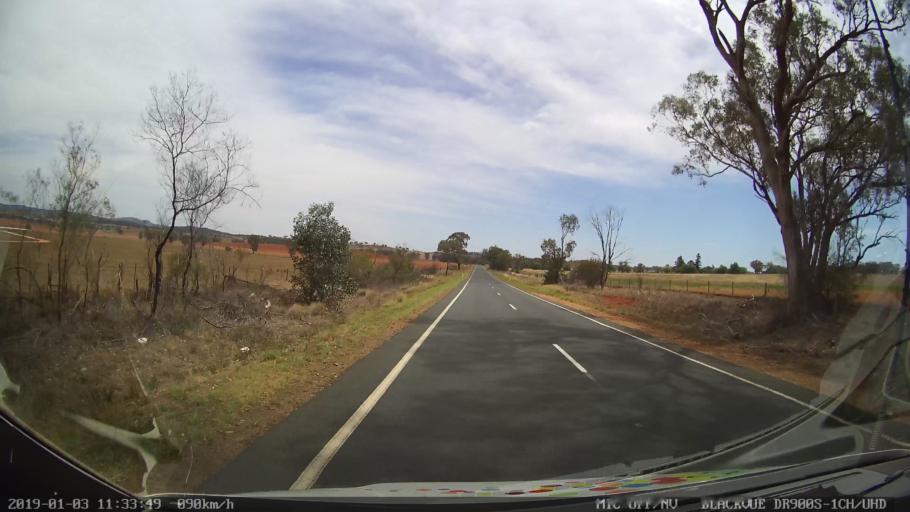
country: AU
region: New South Wales
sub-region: Weddin
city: Grenfell
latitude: -33.9424
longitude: 148.1683
